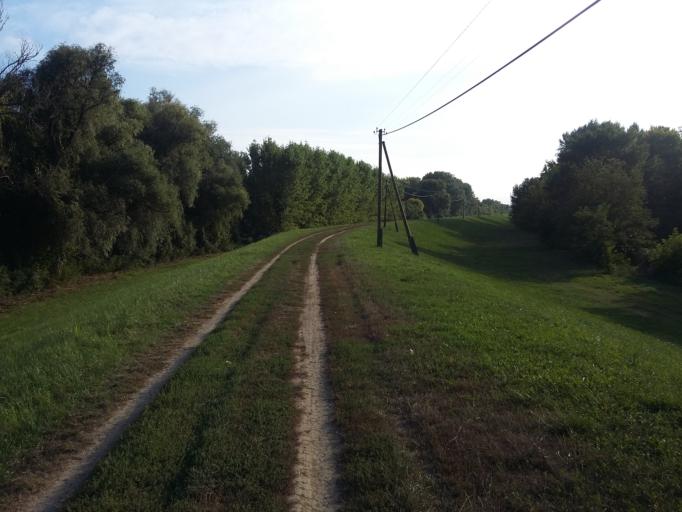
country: HU
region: Csongrad
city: Szeged
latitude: 46.2061
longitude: 20.1170
